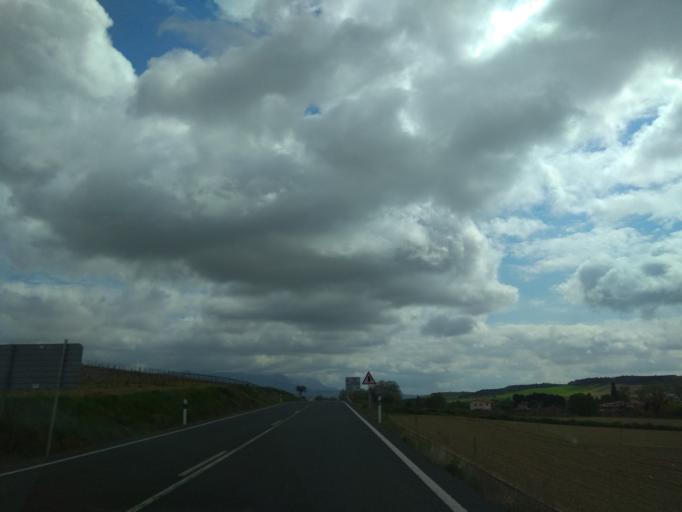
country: ES
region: La Rioja
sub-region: Provincia de La Rioja
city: Ollauri
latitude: 42.5461
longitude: -2.8386
